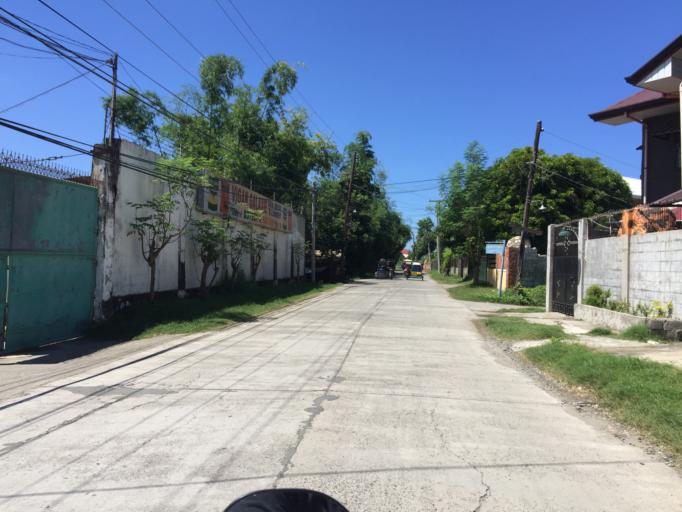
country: PH
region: Ilocos
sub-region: Province of Ilocos Sur
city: Vigan
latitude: 17.5773
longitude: 120.3743
